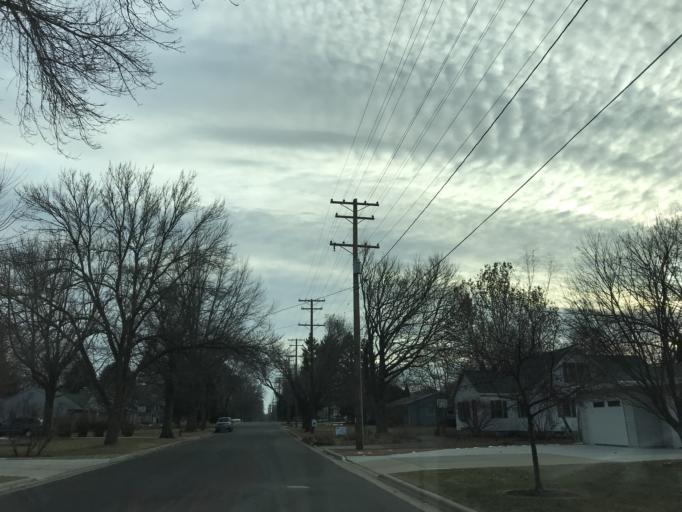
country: US
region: Wisconsin
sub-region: Dane County
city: Monona
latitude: 43.0687
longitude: -89.3334
